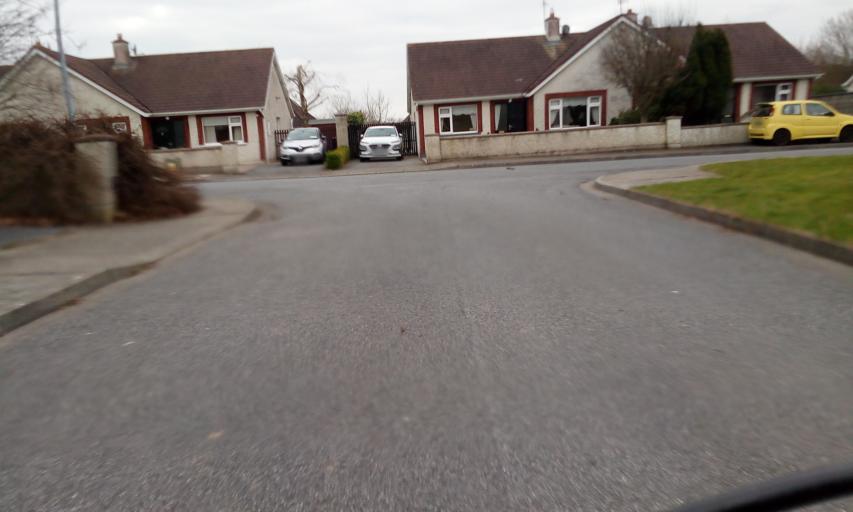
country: IE
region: Leinster
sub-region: Kilkenny
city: Kilkenny
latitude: 52.6617
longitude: -7.2309
